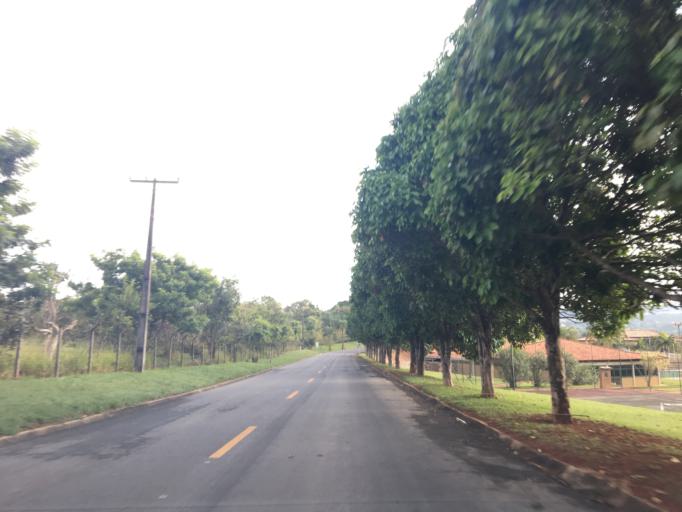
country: BR
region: Federal District
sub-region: Brasilia
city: Brasilia
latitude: -15.7987
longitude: -47.7999
